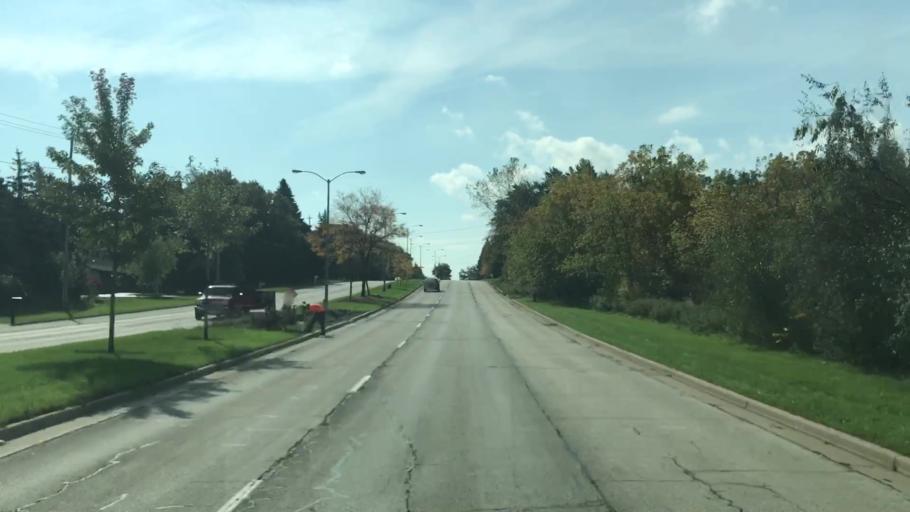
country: US
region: Wisconsin
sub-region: Waukesha County
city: Butler
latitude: 43.1578
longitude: -88.0448
